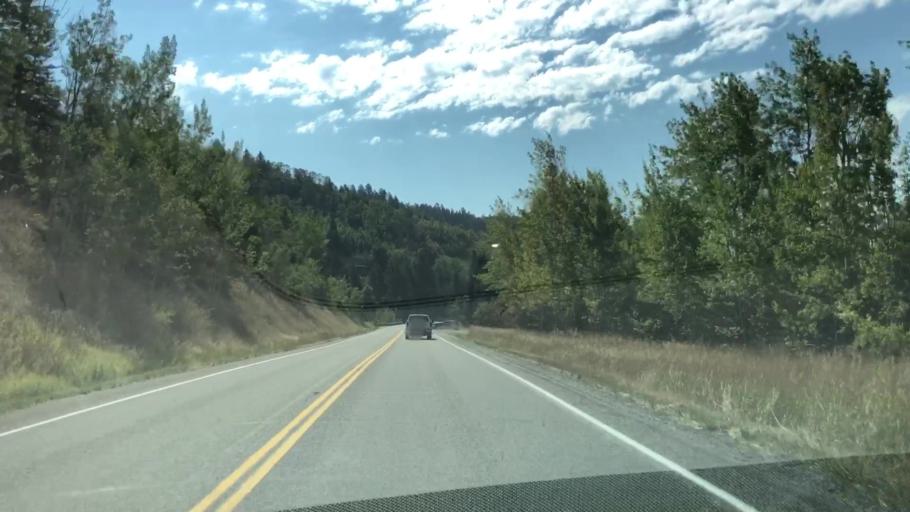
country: US
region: Idaho
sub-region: Teton County
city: Victor
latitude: 43.2795
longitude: -111.1168
